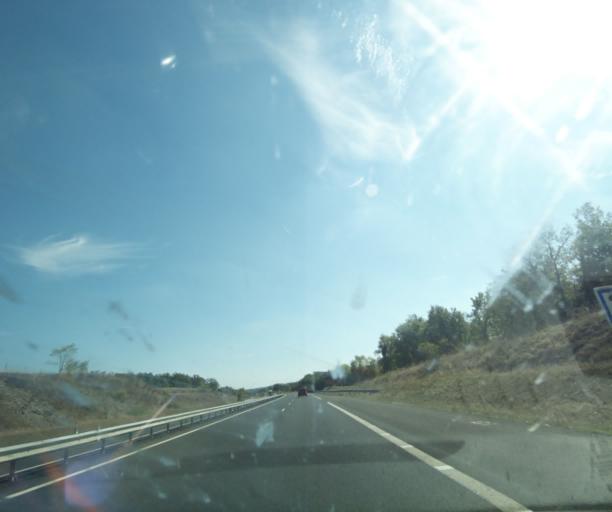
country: FR
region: Limousin
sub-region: Departement de la Correze
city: Brive-la-Gaillarde
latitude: 45.0315
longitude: 1.5272
